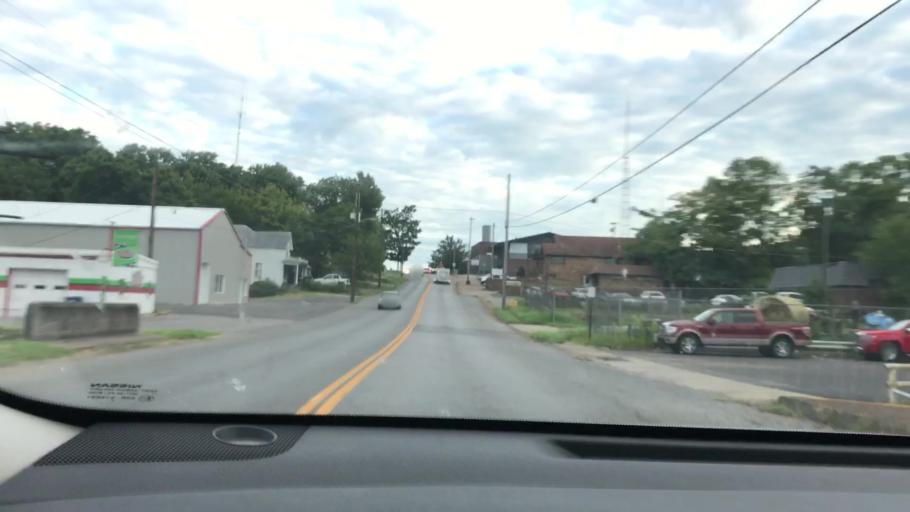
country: US
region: Kentucky
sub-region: Calloway County
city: Murray
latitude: 36.6061
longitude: -88.3022
